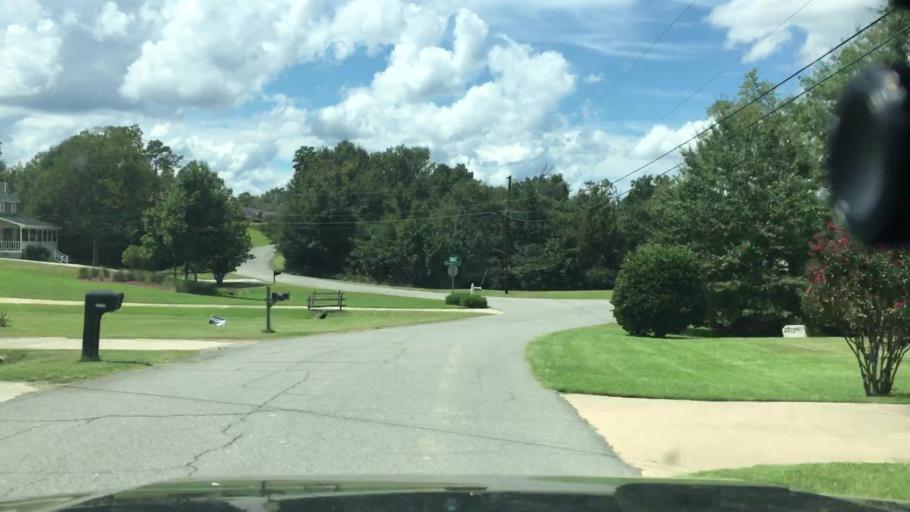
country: US
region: Georgia
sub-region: Bibb County
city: West Point
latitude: 32.8157
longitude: -83.7929
